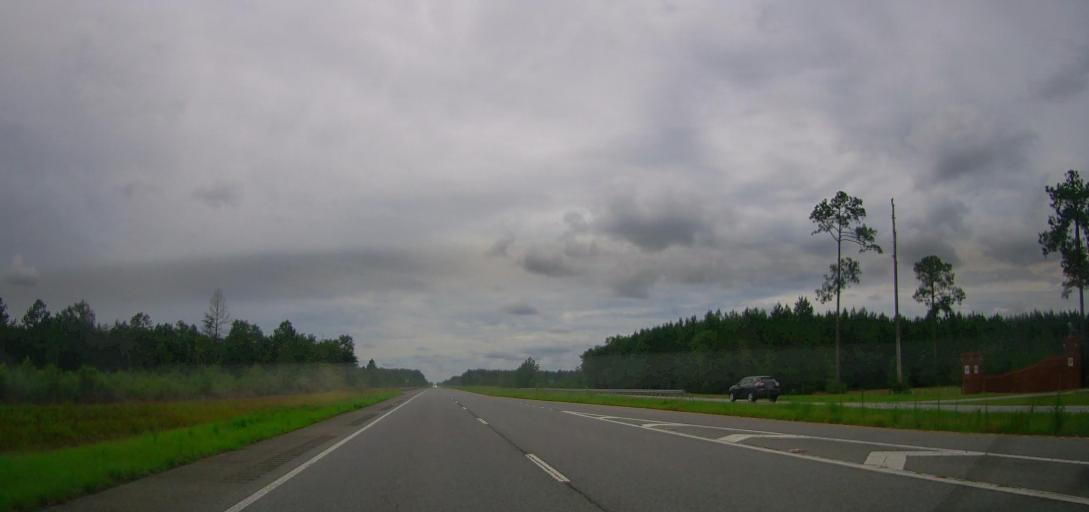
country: US
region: Georgia
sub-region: Appling County
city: Baxley
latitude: 31.7380
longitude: -82.2327
